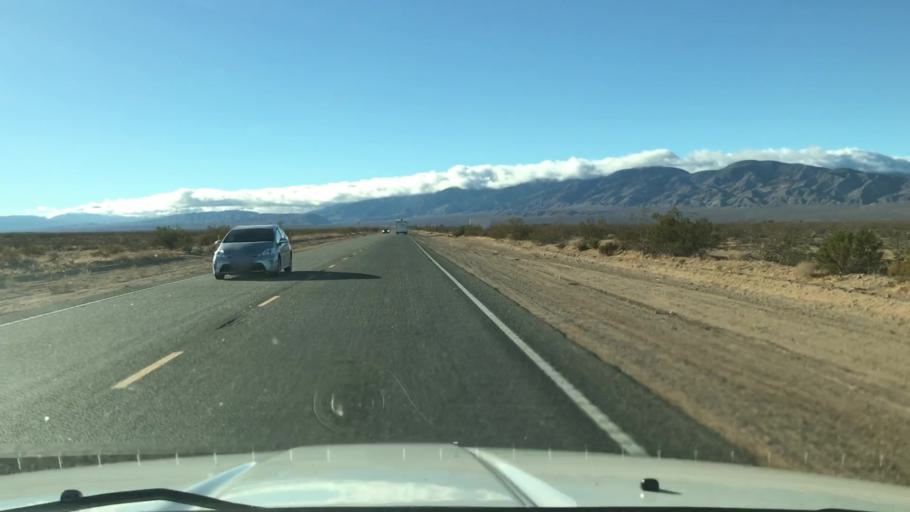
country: US
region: California
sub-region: Kern County
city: California City
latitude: 35.1255
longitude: -118.0656
